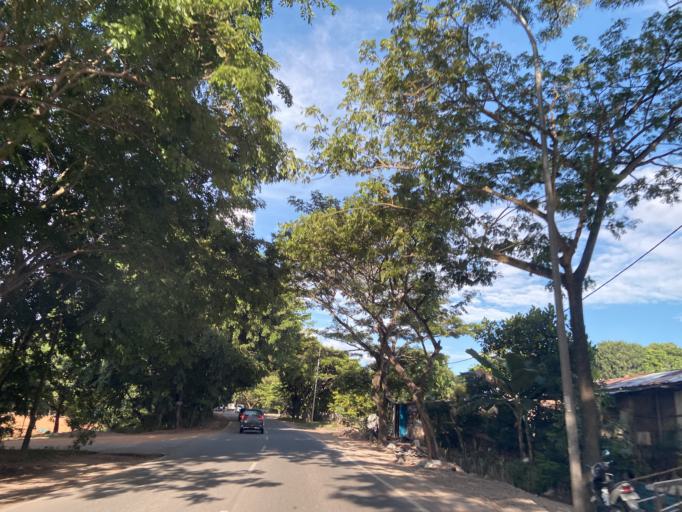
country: SG
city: Singapore
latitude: 1.1222
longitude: 104.0131
